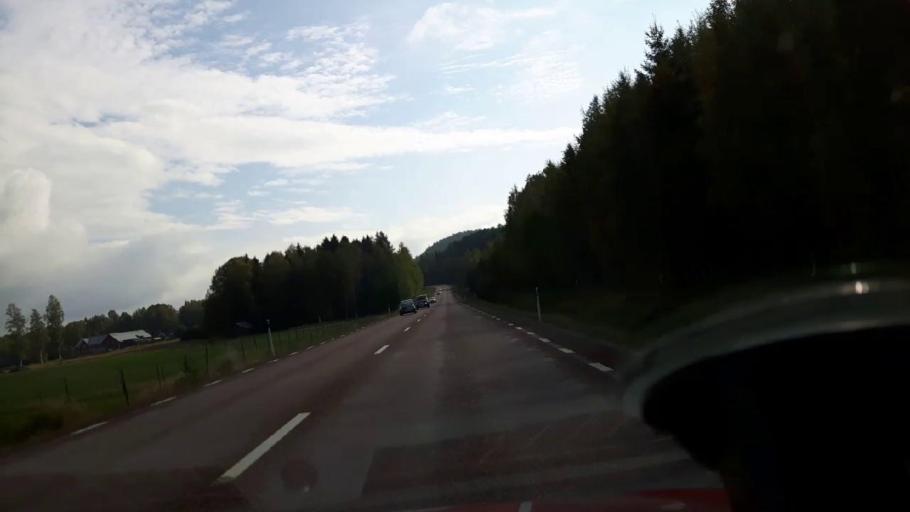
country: SE
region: Gaevleborg
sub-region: Bollnas Kommun
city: Kilafors
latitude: 61.2098
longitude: 16.7415
